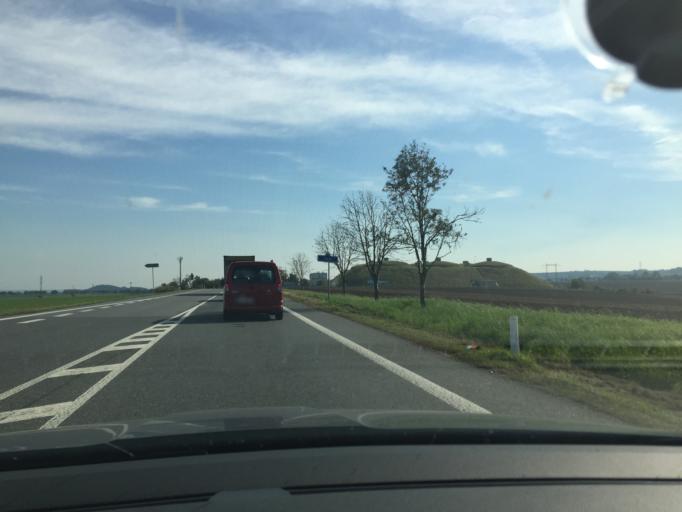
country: CZ
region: Central Bohemia
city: Cerhenice
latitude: 50.0461
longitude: 15.0668
